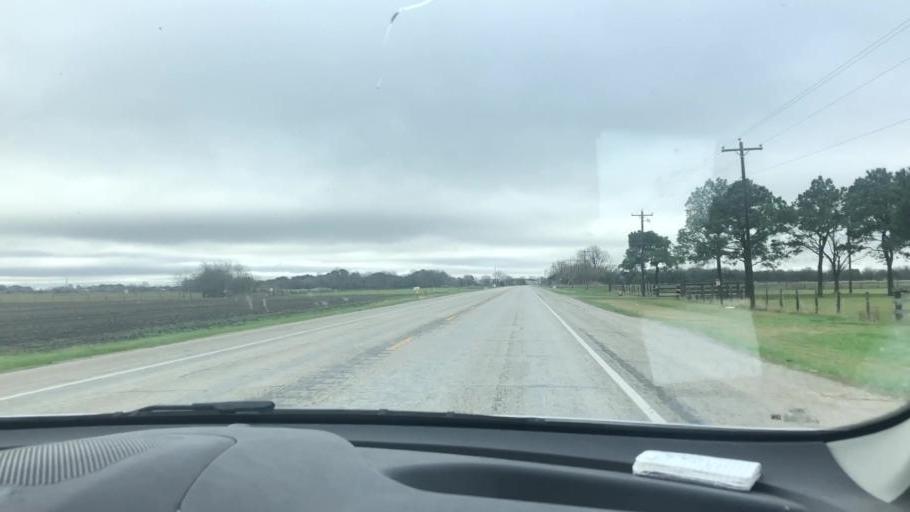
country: US
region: Texas
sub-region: Wharton County
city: Boling
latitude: 29.2238
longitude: -96.0327
